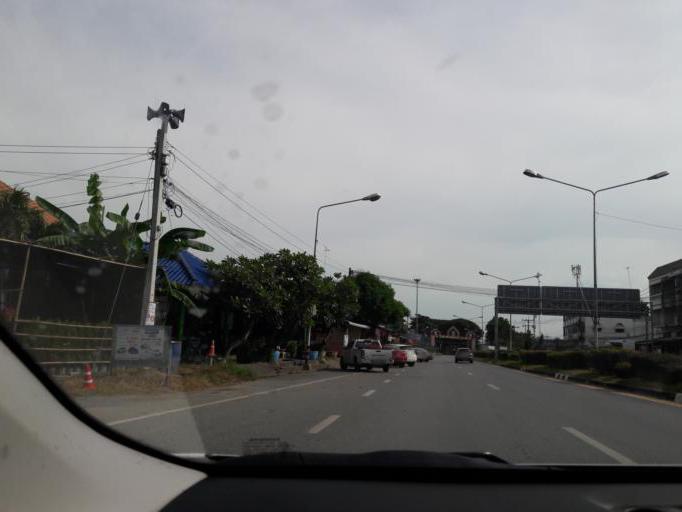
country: TH
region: Ang Thong
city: Ang Thong
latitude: 14.5922
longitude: 100.4452
